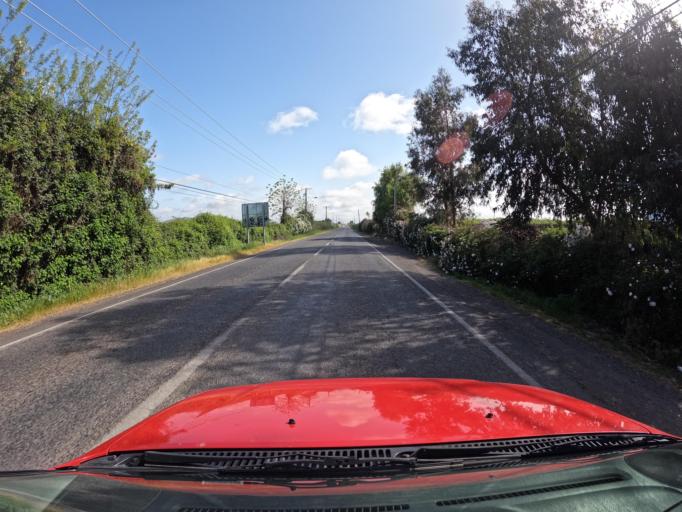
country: CL
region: Maule
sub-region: Provincia de Curico
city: Rauco
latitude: -34.9306
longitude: -71.2765
